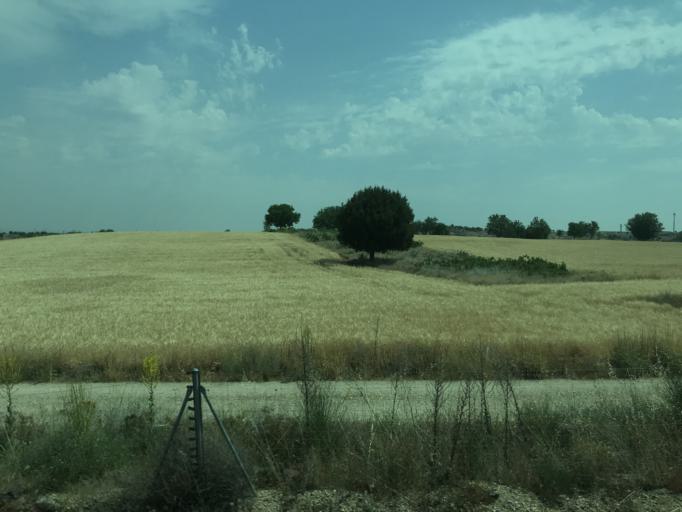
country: ES
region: Castille and Leon
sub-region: Provincia de Burgos
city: Fuentespina
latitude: 41.6284
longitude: -3.6941
